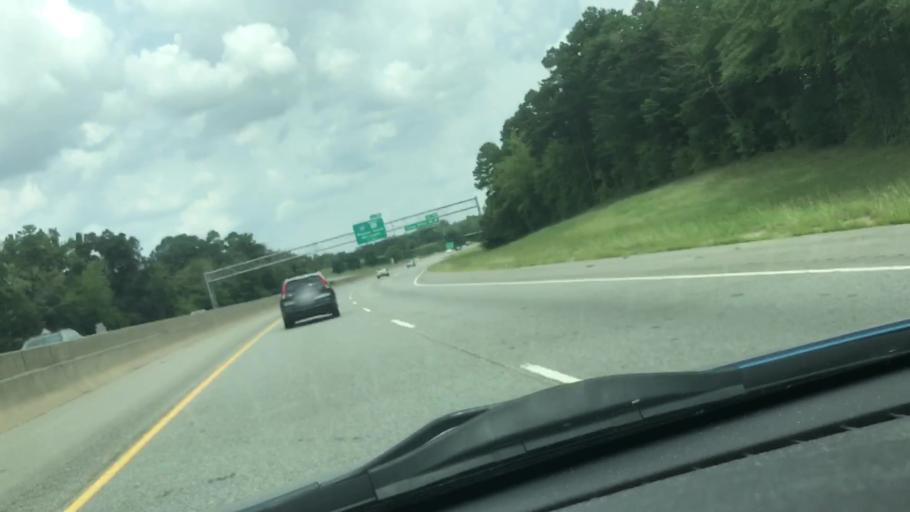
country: US
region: North Carolina
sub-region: Guilford County
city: Greensboro
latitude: 36.0222
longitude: -79.8260
